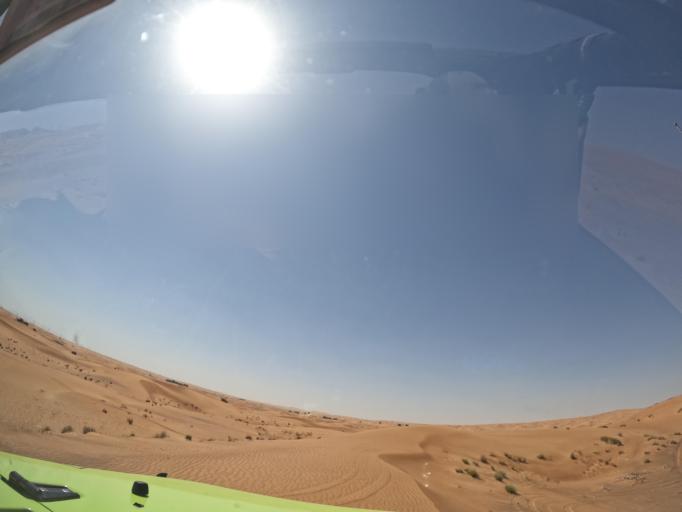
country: AE
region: Ash Shariqah
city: Adh Dhayd
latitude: 25.0195
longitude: 55.7440
